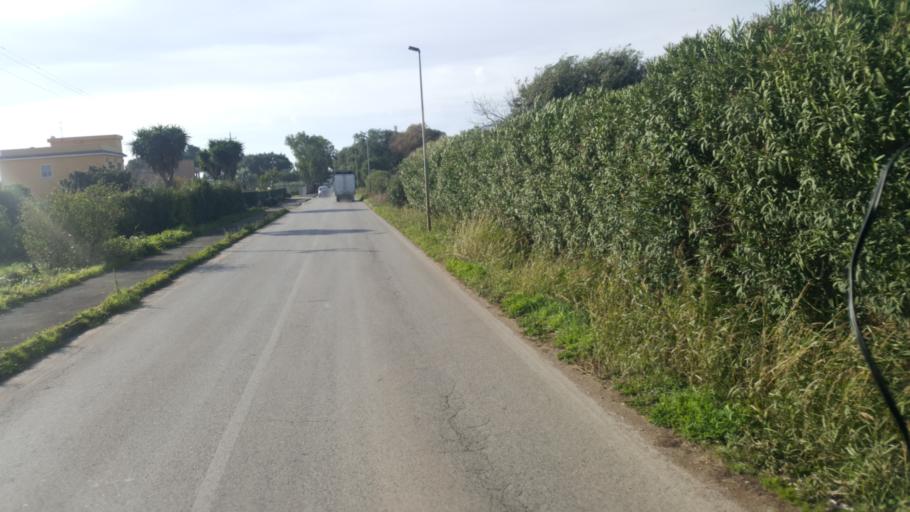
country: IT
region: Latium
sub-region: Provincia di Latina
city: Casalazzara
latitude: 41.6264
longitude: 12.5892
